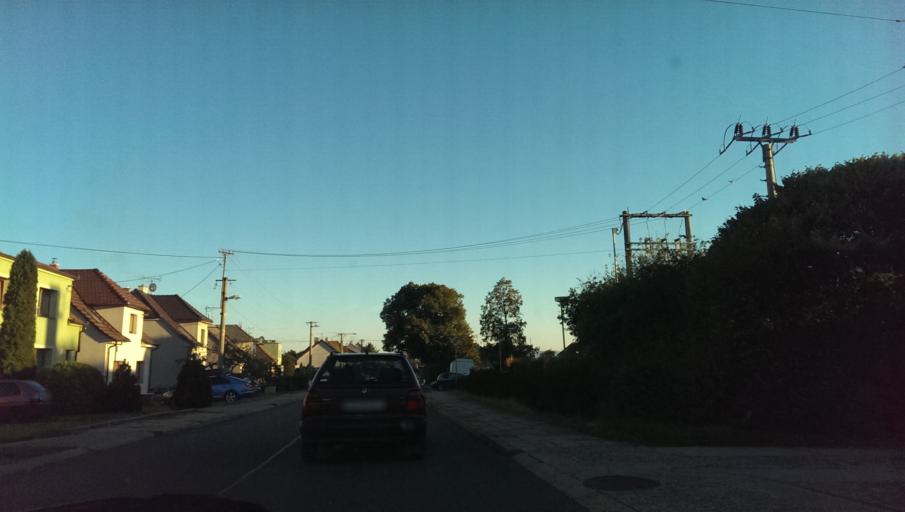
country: CZ
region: Zlin
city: Zlechov
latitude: 49.0796
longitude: 17.3768
